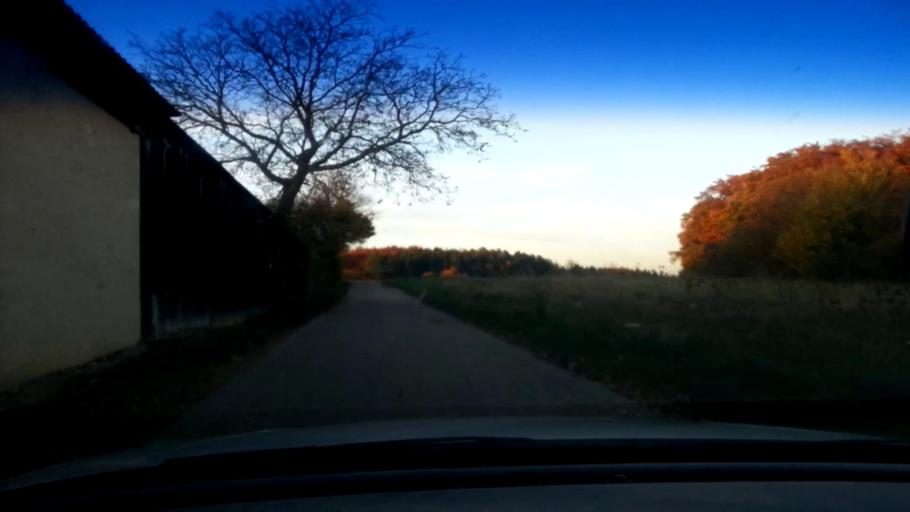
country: DE
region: Bavaria
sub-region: Upper Franconia
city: Heiligenstadt
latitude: 49.8583
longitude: 11.1157
